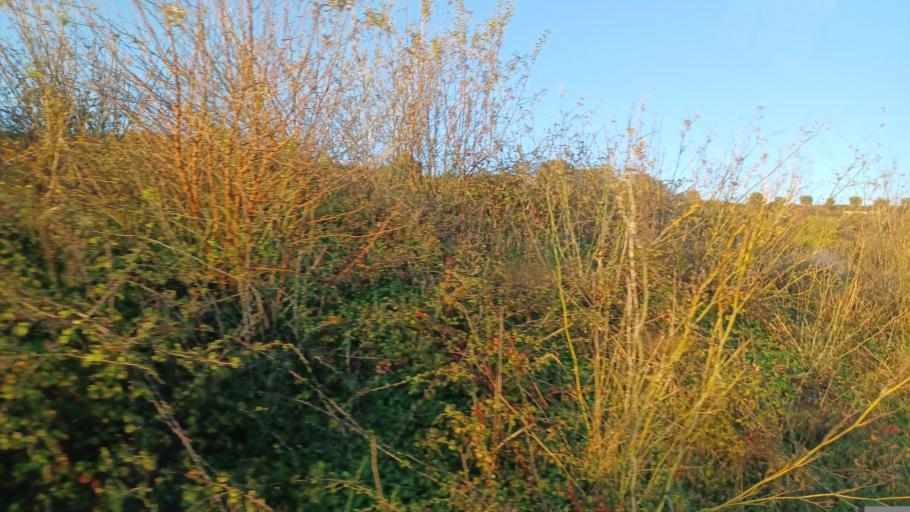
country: CY
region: Pafos
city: Mesogi
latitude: 34.8649
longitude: 32.5106
